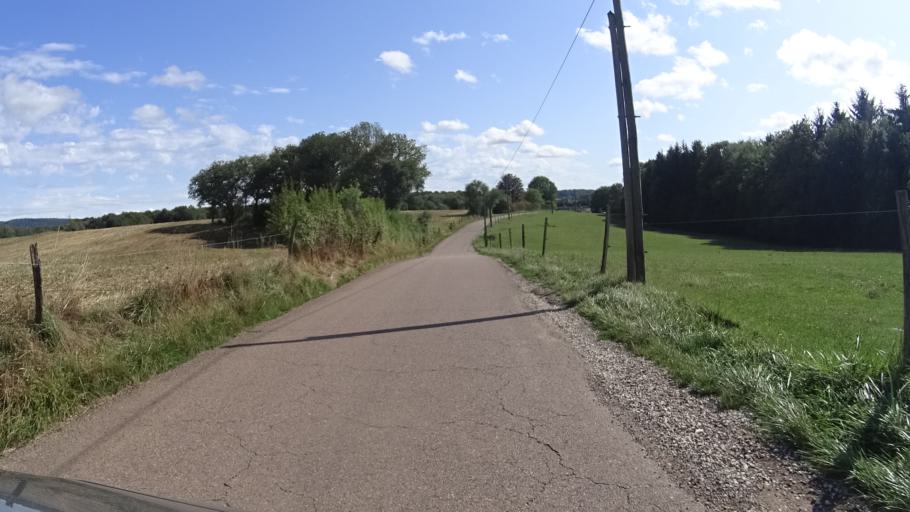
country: FR
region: Franche-Comte
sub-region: Departement du Doubs
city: Saone
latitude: 47.2133
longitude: 6.1118
